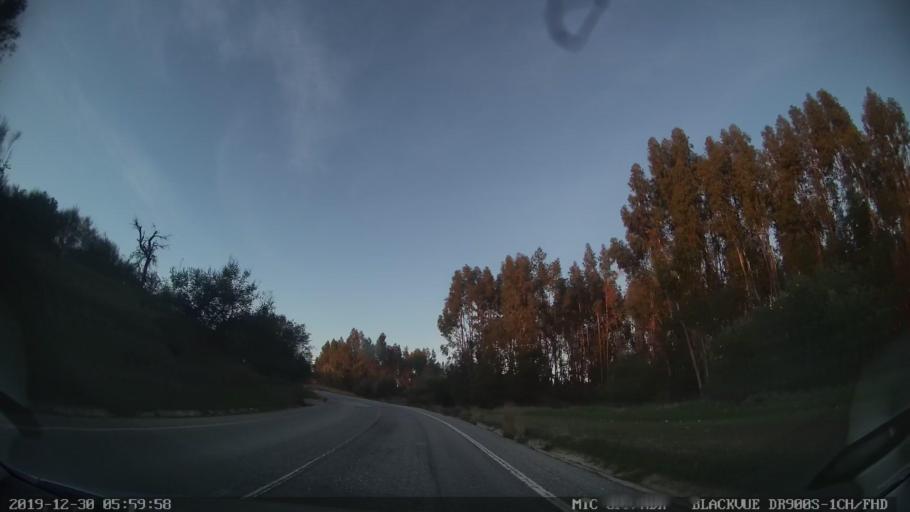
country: PT
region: Castelo Branco
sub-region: Idanha-A-Nova
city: Idanha-a-Nova
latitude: 40.0484
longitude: -7.2438
